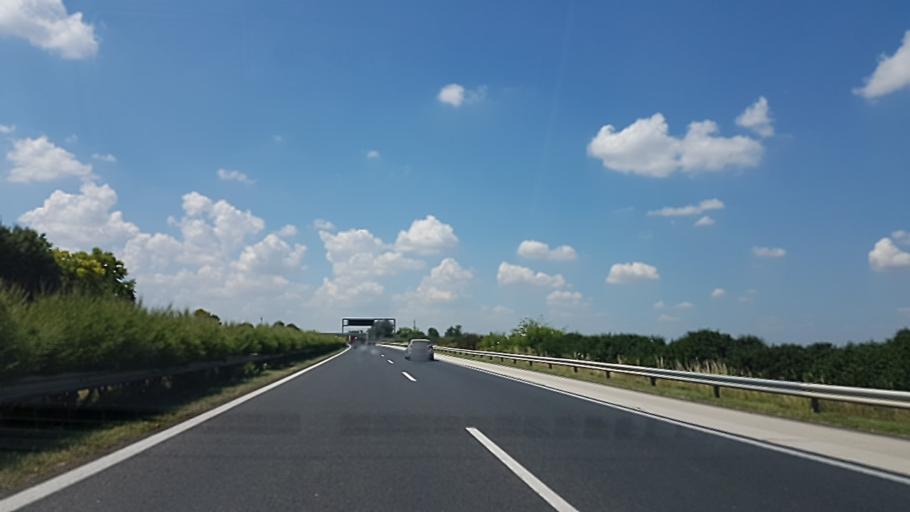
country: HU
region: Komarom-Esztergom
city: Mocsa
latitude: 47.6548
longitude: 18.1935
